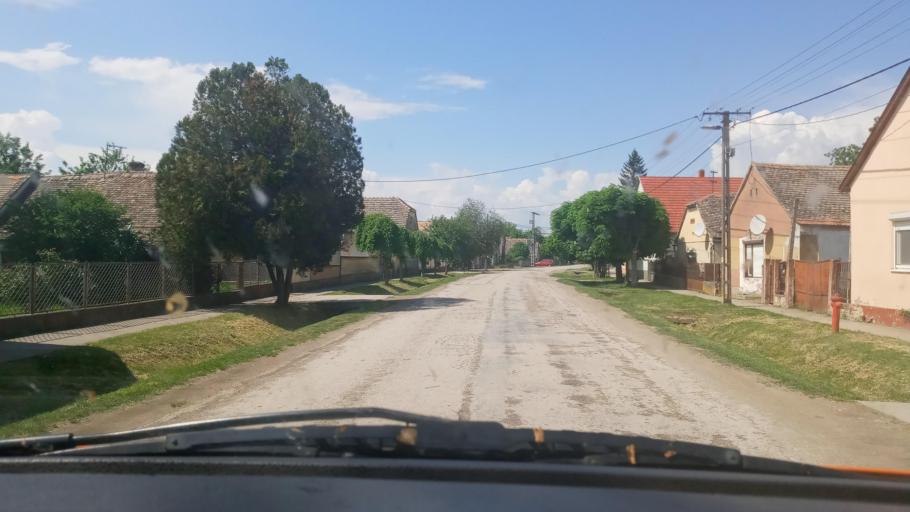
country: HU
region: Baranya
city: Beremend
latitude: 45.7895
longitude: 18.3517
